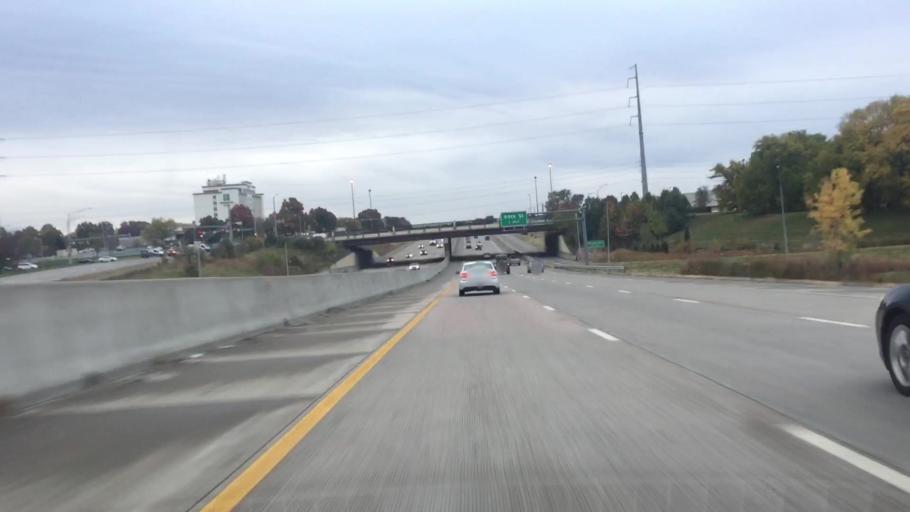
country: US
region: Kansas
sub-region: Johnson County
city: Lenexa
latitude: 38.9728
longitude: -94.7168
